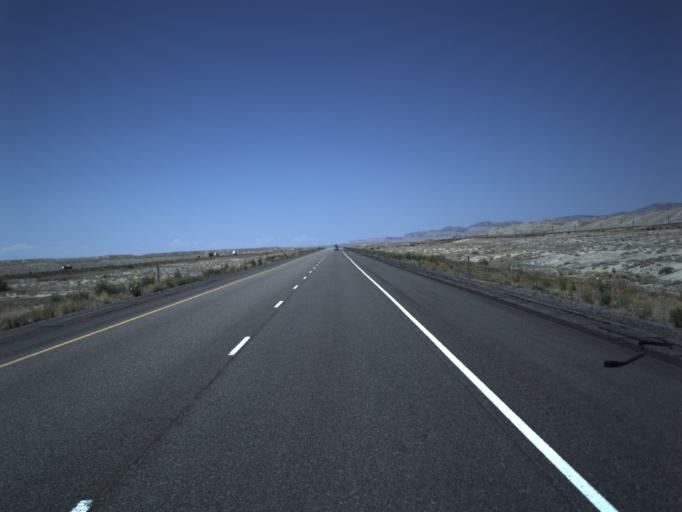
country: US
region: Utah
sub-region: Grand County
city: Moab
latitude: 38.9338
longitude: -109.4418
